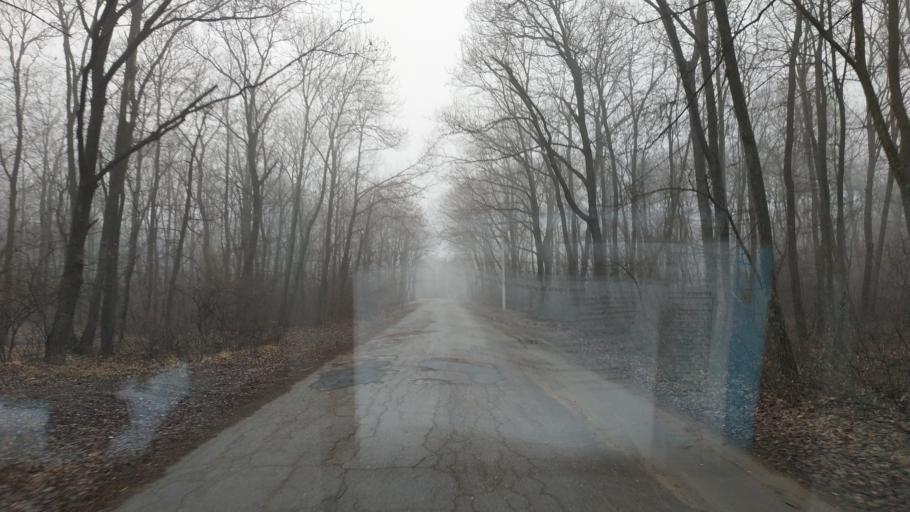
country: MD
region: Laloveni
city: Ialoveni
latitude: 46.9461
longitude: 28.7021
